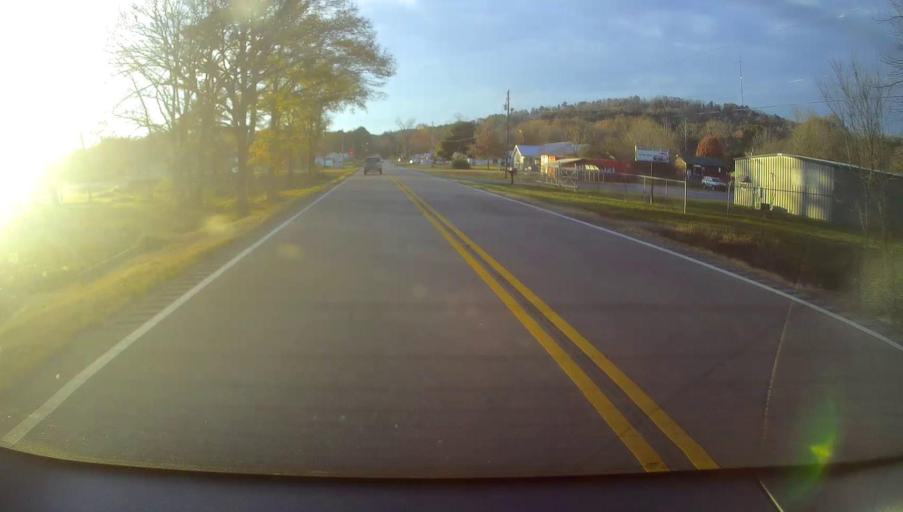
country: US
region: Alabama
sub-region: Saint Clair County
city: Steele
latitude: 34.0671
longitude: -86.3005
